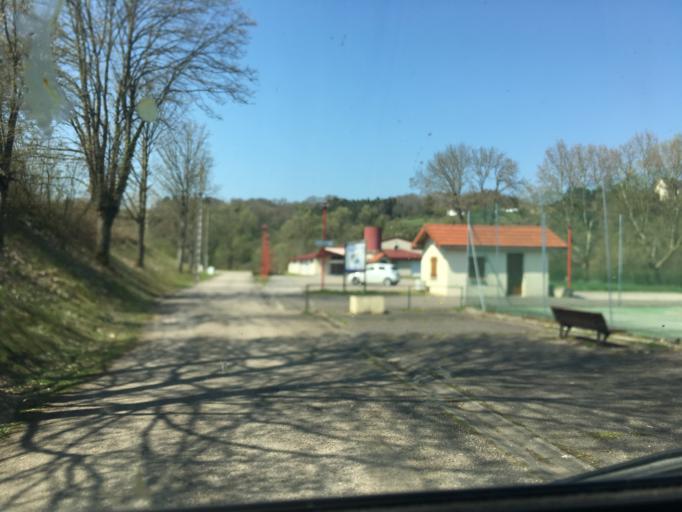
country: FR
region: Lorraine
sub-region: Departement de la Meuse
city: Vigneulles-les-Hattonchatel
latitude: 48.9520
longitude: 5.8612
